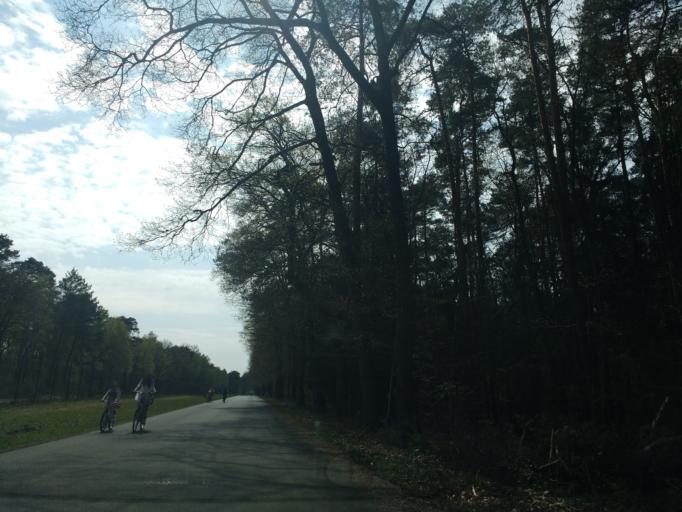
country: DE
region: North Rhine-Westphalia
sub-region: Regierungsbezirk Detmold
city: Hovelhof
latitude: 51.7899
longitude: 8.7205
